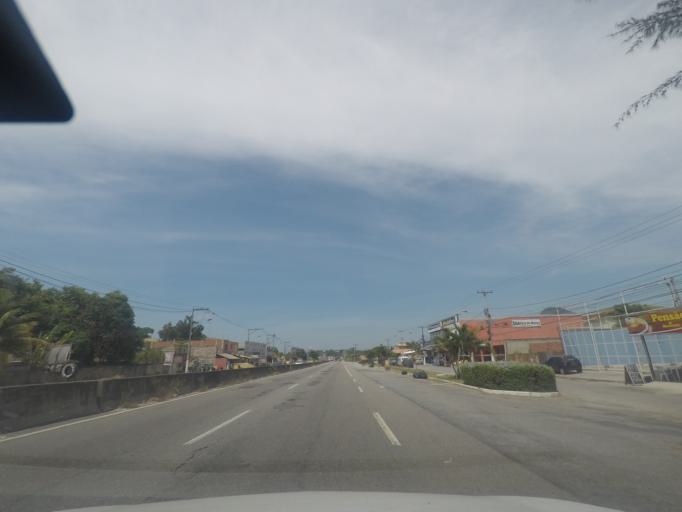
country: BR
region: Rio de Janeiro
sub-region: Marica
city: Marica
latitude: -22.9259
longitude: -42.8654
